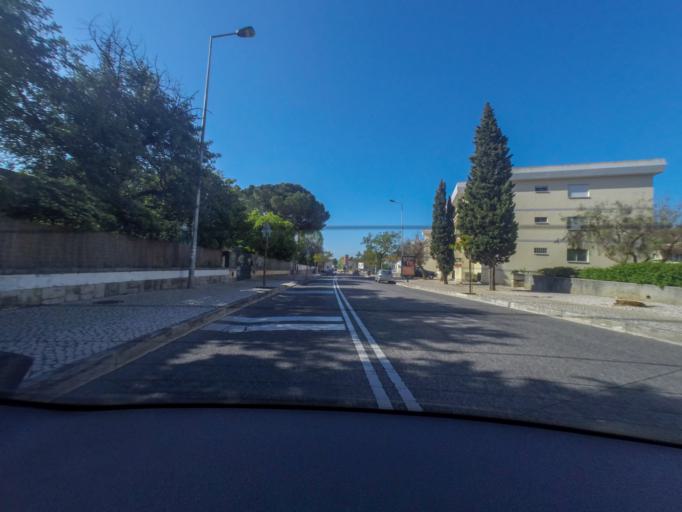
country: PT
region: Lisbon
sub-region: Cascais
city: Monte Estoril
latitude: 38.7045
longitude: -9.4177
